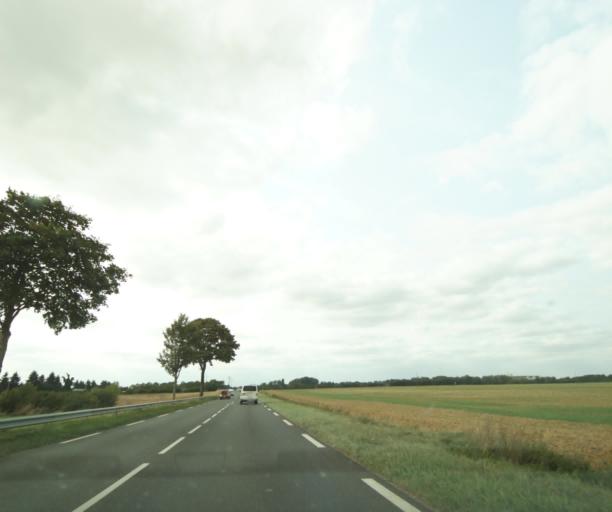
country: FR
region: Centre
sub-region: Departement d'Indre-et-Loire
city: Reignac-sur-Indre
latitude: 47.2043
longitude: 0.9085
